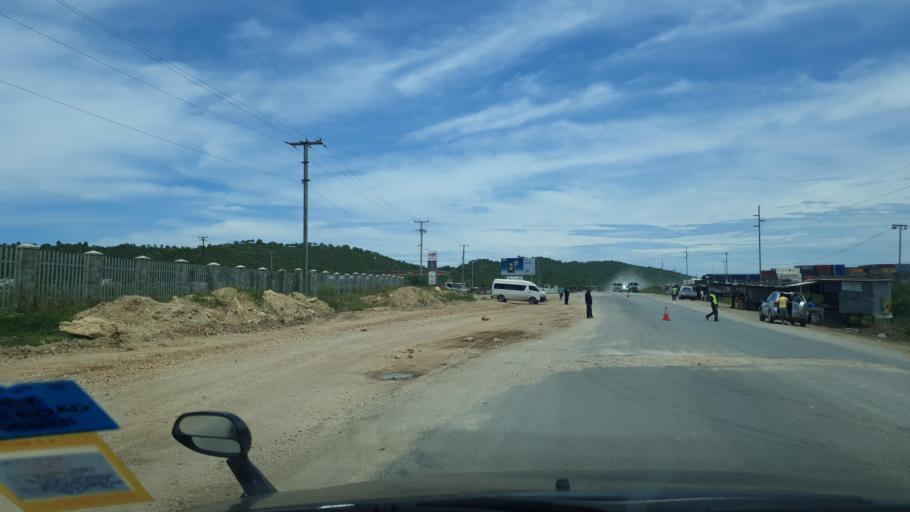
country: PG
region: National Capital
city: Port Moresby
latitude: -9.4196
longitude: 147.0792
